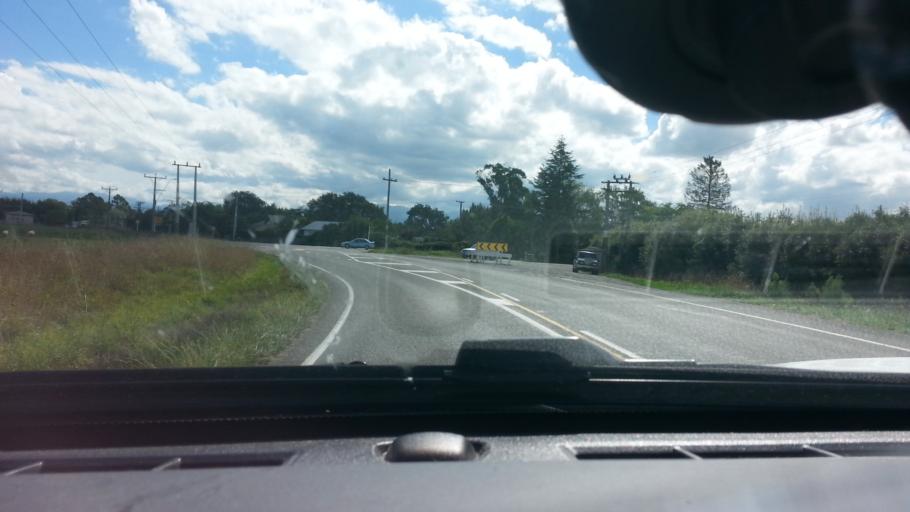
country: NZ
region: Wellington
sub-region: Masterton District
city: Masterton
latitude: -40.9501
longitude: 175.6975
